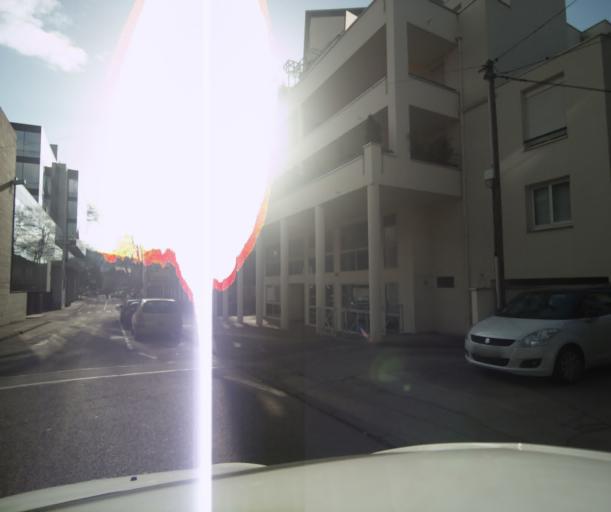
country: FR
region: Franche-Comte
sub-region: Departement du Doubs
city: Besancon
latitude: 47.2440
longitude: 6.0299
